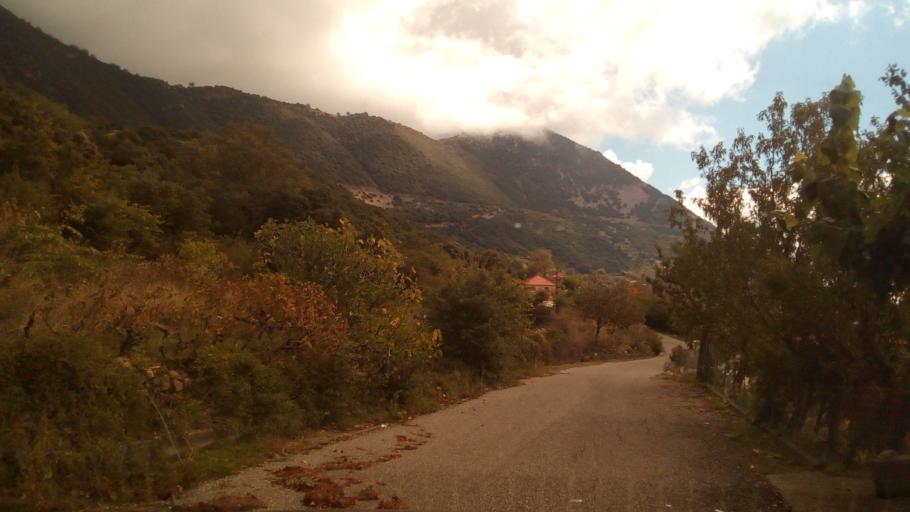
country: GR
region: West Greece
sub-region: Nomos Aitolias kai Akarnanias
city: Nafpaktos
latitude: 38.4977
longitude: 21.8431
